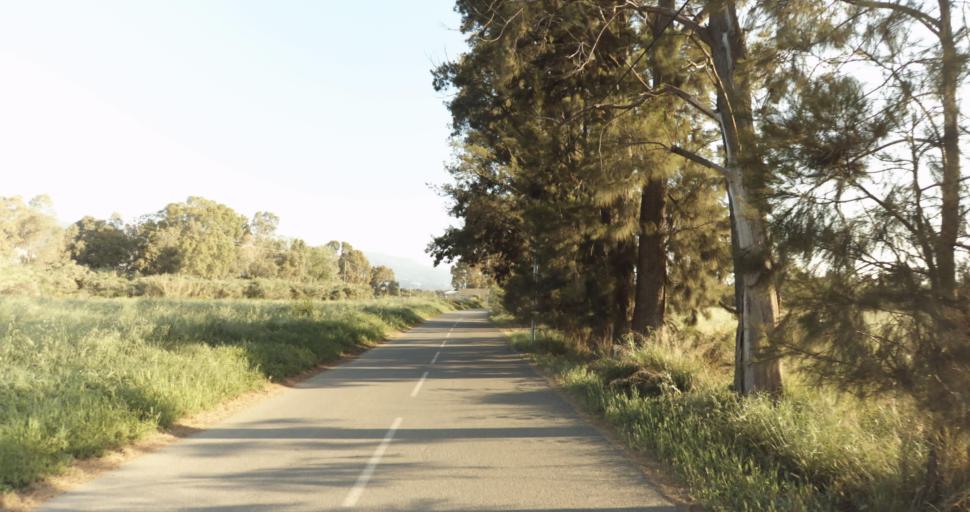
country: FR
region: Corsica
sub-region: Departement de la Haute-Corse
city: Biguglia
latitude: 42.6142
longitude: 9.4441
